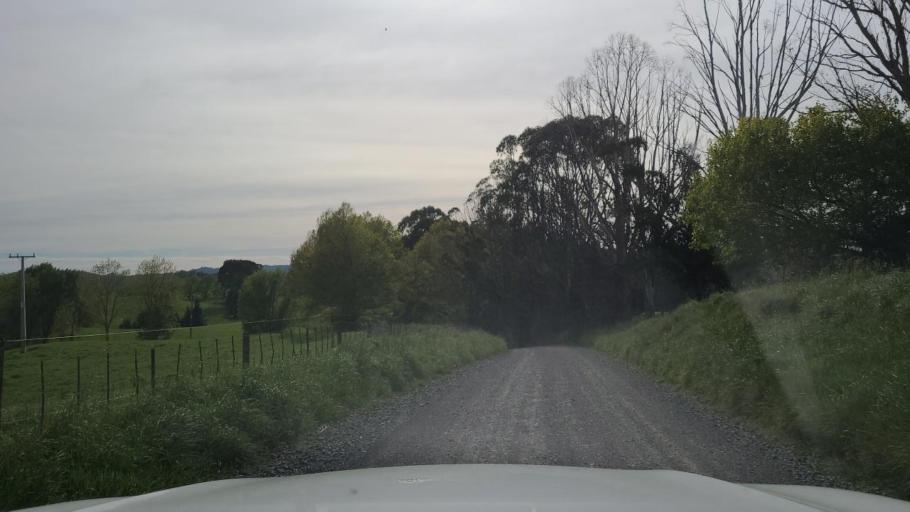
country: NZ
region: Hawke's Bay
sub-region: Napier City
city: Taradale
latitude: -39.3027
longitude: 176.6329
